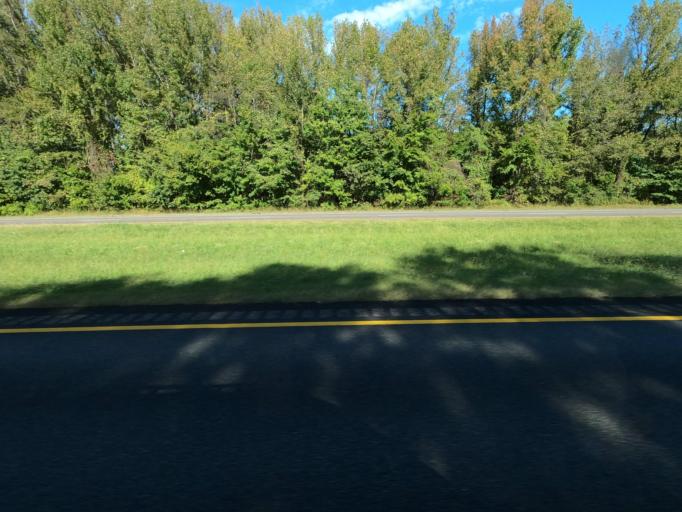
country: US
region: Tennessee
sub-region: Tipton County
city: Mason
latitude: 35.3690
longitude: -89.4744
